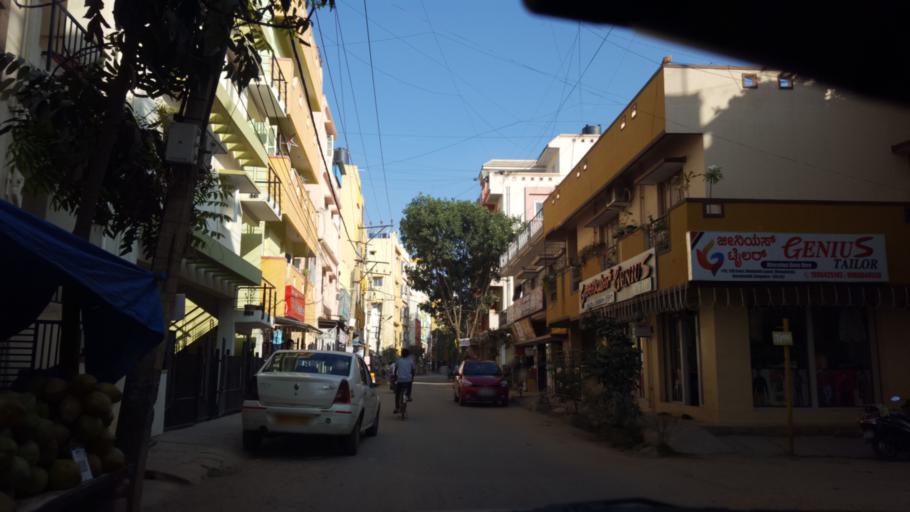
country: IN
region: Karnataka
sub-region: Bangalore Urban
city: Bangalore
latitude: 12.9497
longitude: 77.7130
